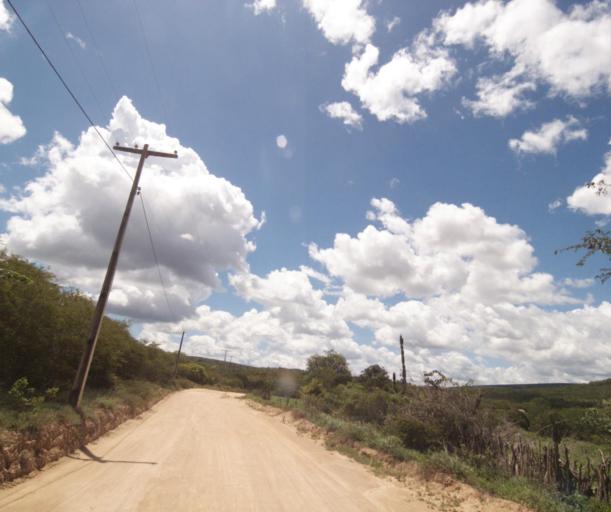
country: BR
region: Bahia
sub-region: Pocoes
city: Pocoes
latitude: -14.3808
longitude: -40.5586
